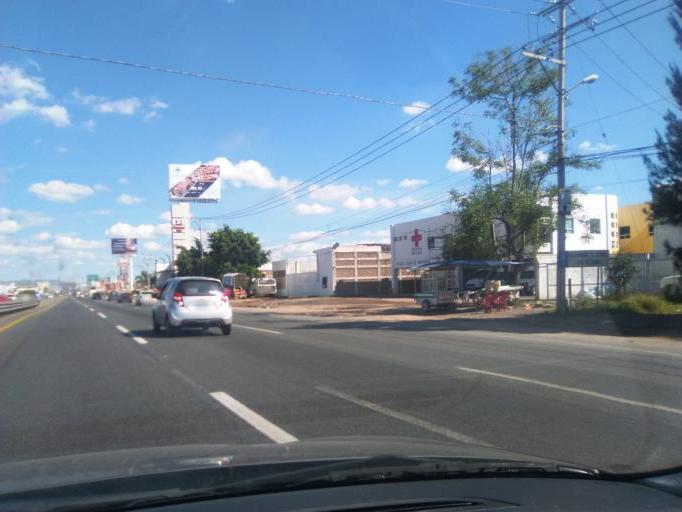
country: MX
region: Guanajuato
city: Silao
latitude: 20.9557
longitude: -101.4344
